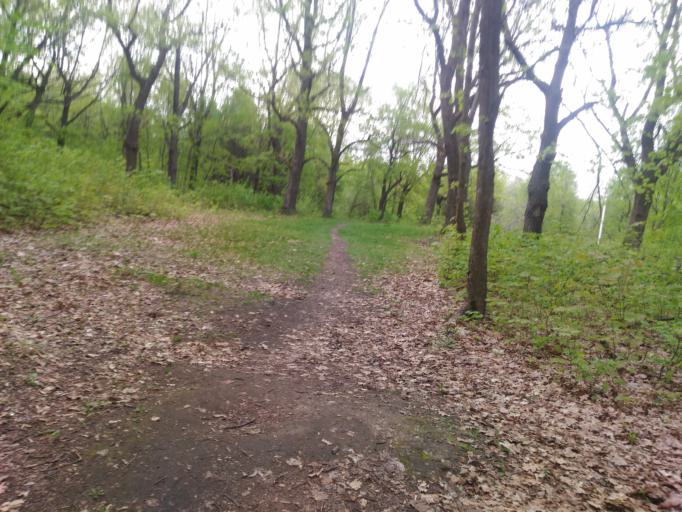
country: RU
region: Ulyanovsk
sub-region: Ulyanovskiy Rayon
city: Ulyanovsk
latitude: 54.2735
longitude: 48.3513
